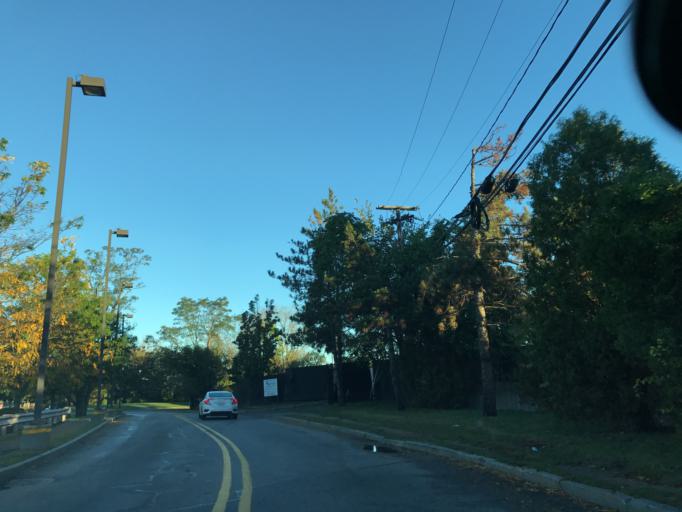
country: US
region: Massachusetts
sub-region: Norfolk County
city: Dedham
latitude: 42.2549
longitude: -71.1669
